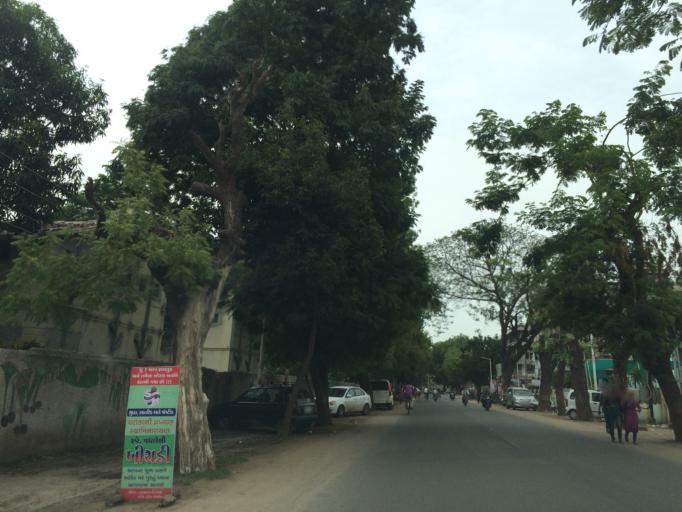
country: IN
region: Gujarat
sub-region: Anand
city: Anand
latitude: 22.5525
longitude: 72.9286
